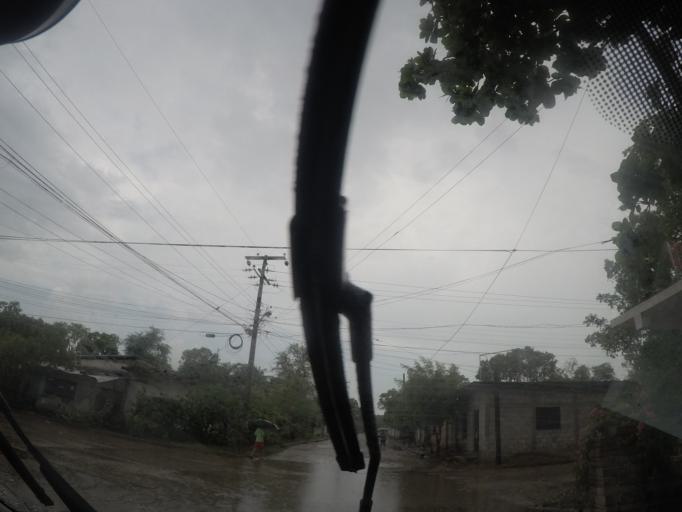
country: MX
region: Oaxaca
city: San Pedro Tapanatepec
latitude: 16.3646
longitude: -94.1972
